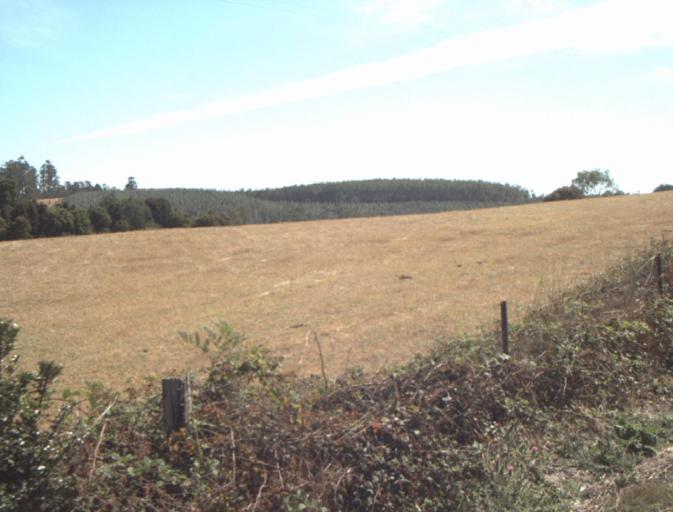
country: AU
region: Tasmania
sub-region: Launceston
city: Mayfield
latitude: -41.2315
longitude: 147.2435
